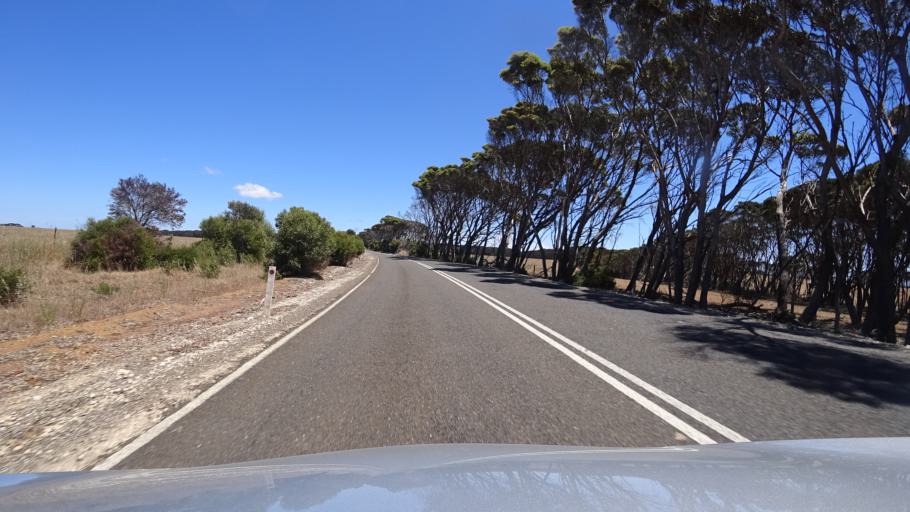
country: AU
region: South Australia
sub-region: Kangaroo Island
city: Kingscote
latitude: -35.7369
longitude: 137.9788
